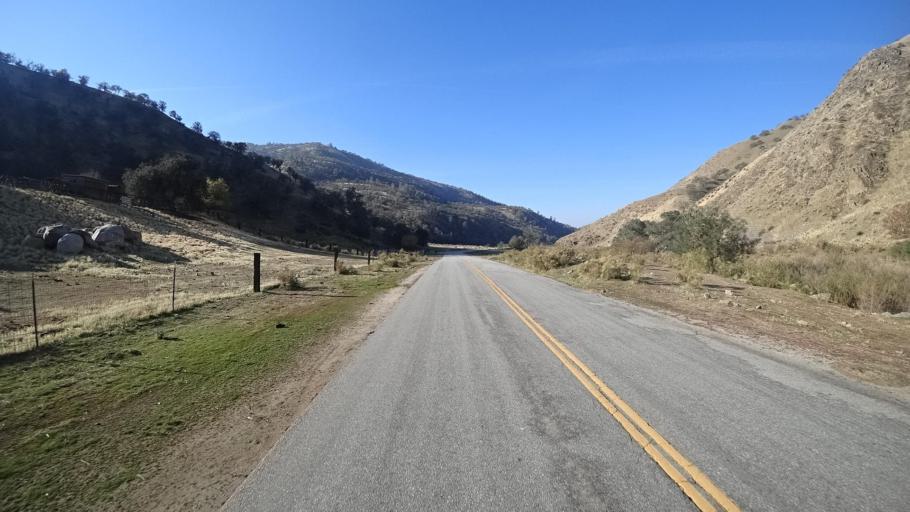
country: US
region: California
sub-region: Kern County
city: Bear Valley Springs
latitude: 35.3142
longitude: -118.5548
